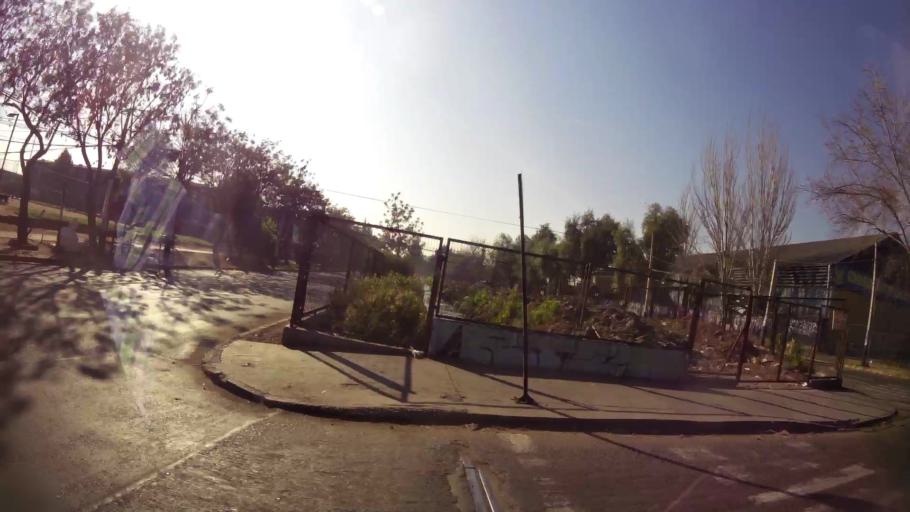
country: CL
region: Santiago Metropolitan
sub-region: Provincia de Santiago
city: Lo Prado
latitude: -33.4655
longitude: -70.7536
